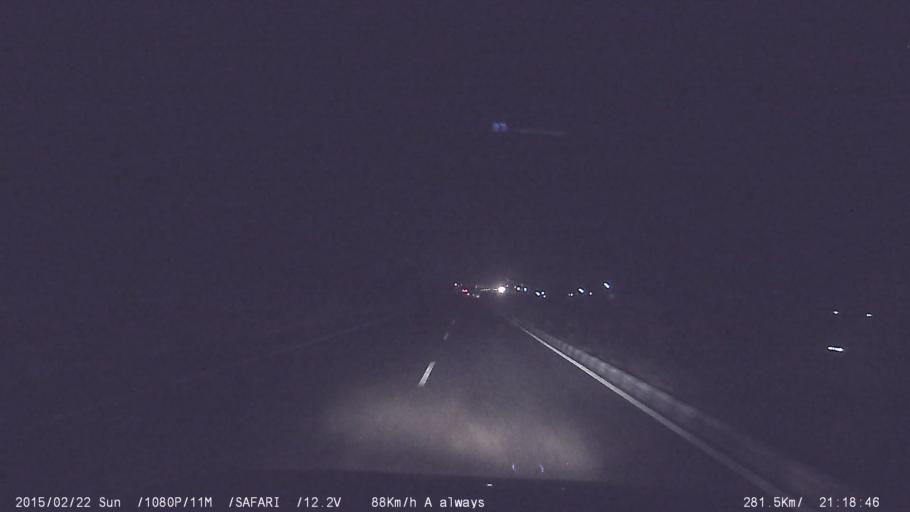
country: IN
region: Tamil Nadu
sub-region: Karur
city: Pallappatti
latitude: 10.8413
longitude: 77.9672
